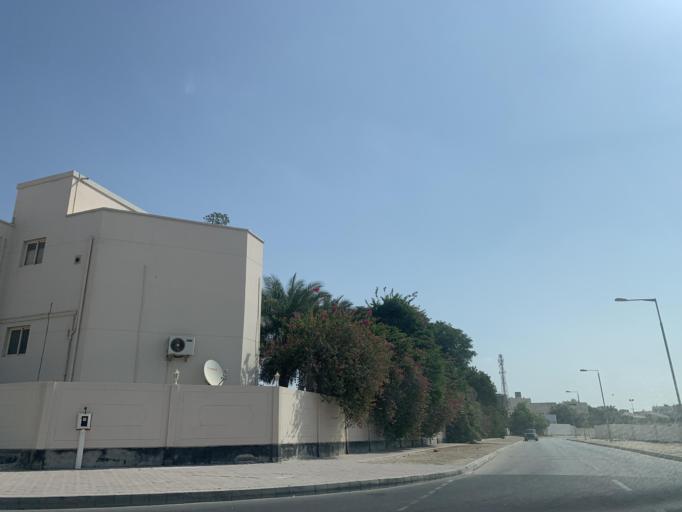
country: BH
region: Central Governorate
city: Madinat Hamad
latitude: 26.1290
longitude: 50.5031
